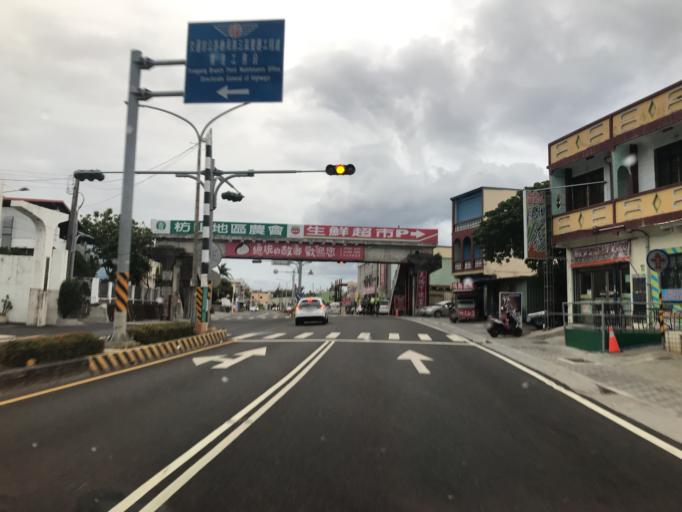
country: TW
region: Taiwan
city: Hengchun
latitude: 22.1916
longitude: 120.6917
